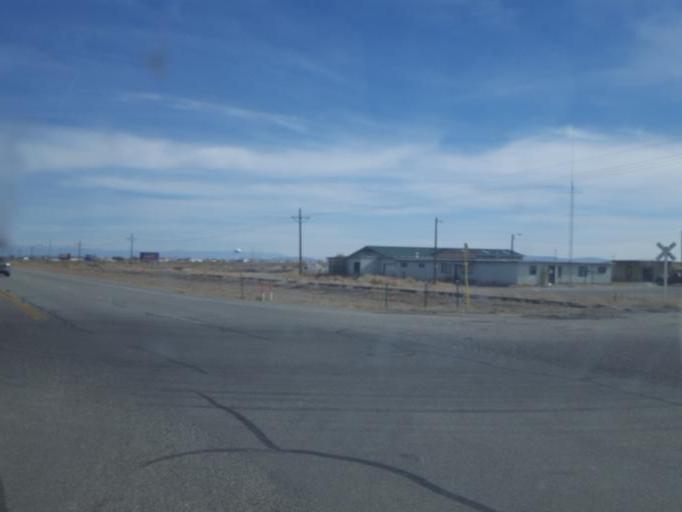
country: US
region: Colorado
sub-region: Alamosa County
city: Alamosa
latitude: 37.4826
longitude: -105.9121
